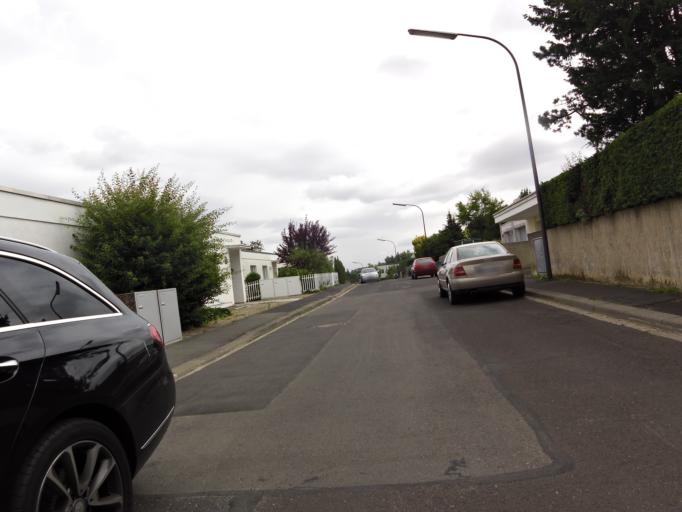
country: DE
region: Bavaria
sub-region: Regierungsbezirk Unterfranken
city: Reichenberg
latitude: 49.7675
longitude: 9.9207
